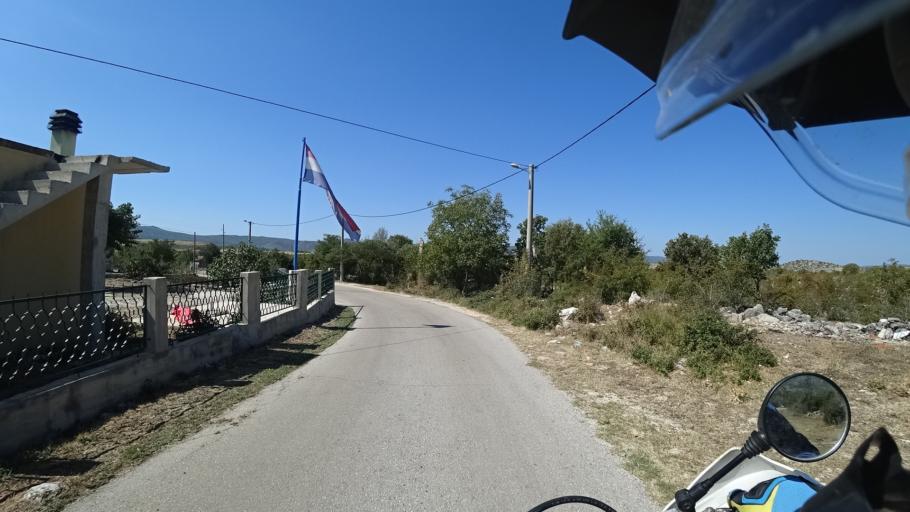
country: HR
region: Sibensko-Kniniska
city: Drnis
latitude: 43.8090
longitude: 16.3417
